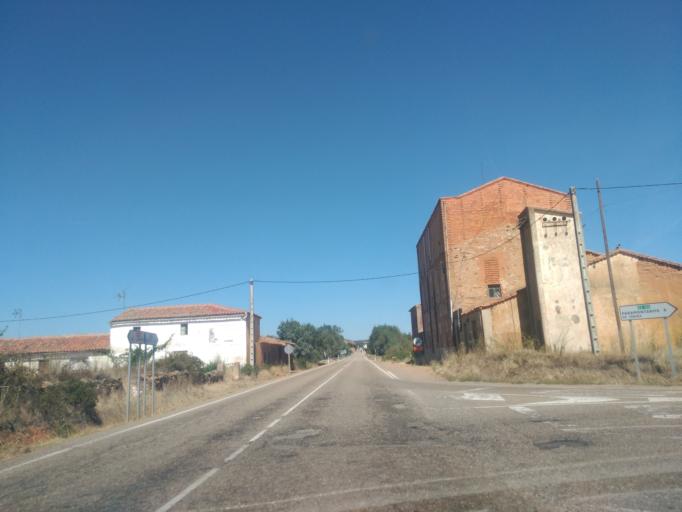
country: ES
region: Castille and Leon
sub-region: Provincia de Zamora
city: Tabara
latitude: 41.8214
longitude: -5.9506
